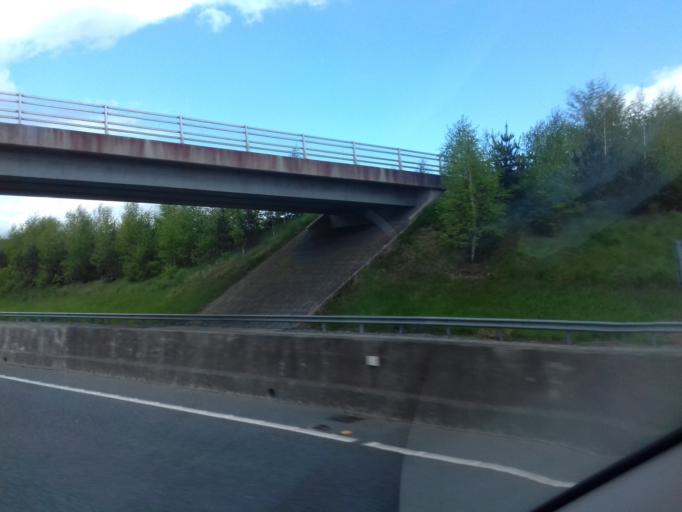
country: IE
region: Leinster
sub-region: Kilkenny
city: Thomastown
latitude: 52.5375
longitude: -7.2479
